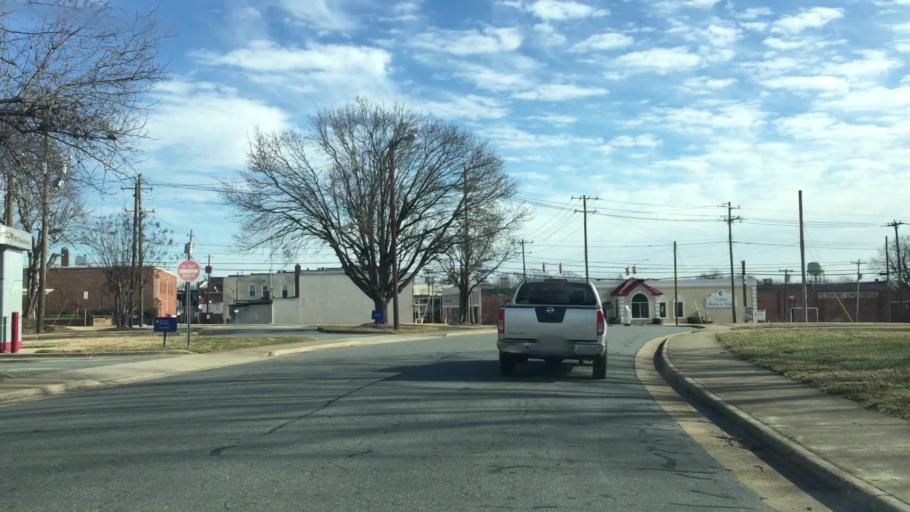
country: US
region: North Carolina
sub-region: Rockingham County
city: Reidsville
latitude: 36.3591
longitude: -79.6668
